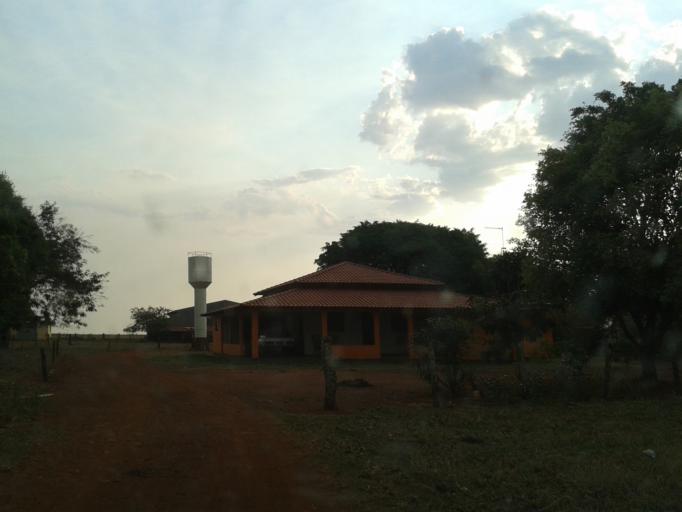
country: BR
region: Minas Gerais
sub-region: Capinopolis
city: Capinopolis
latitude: -18.7647
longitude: -49.7243
